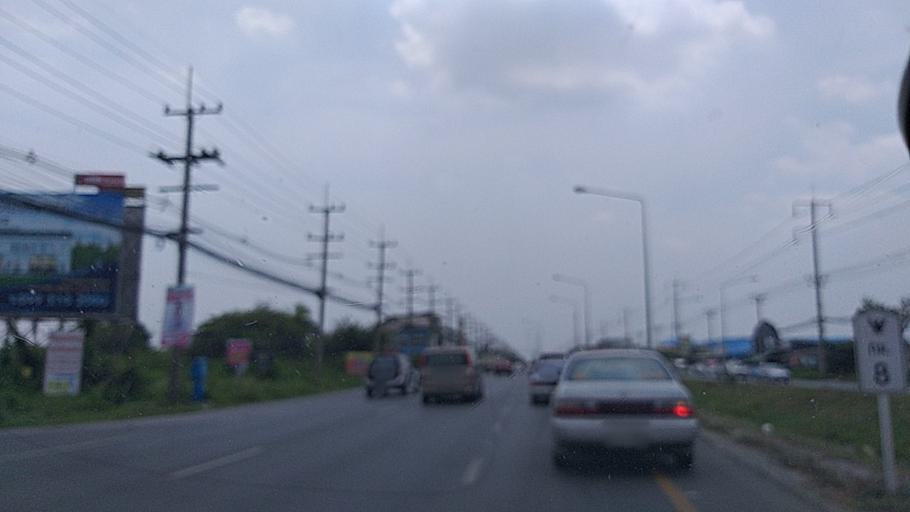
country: TH
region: Nakhon Pathom
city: Salaya
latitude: 13.7788
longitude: 100.3024
